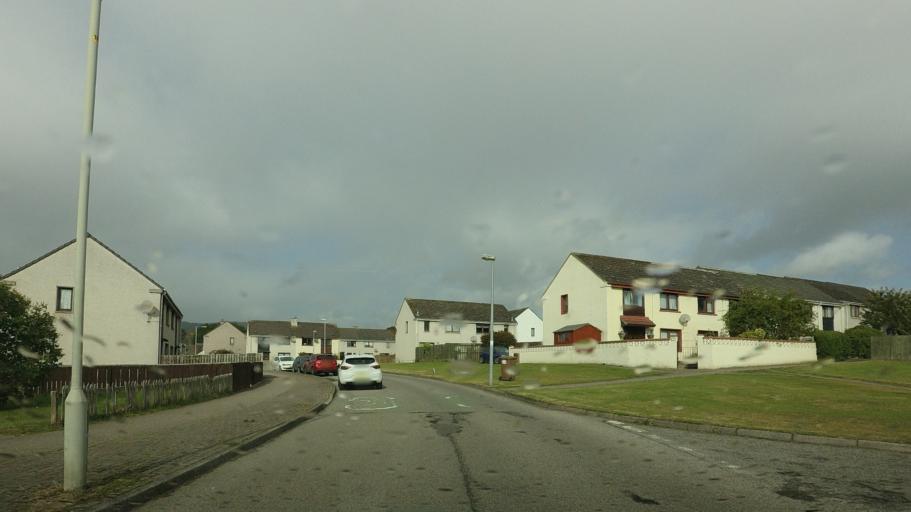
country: GB
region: Scotland
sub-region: Highland
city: Alness
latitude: 57.6944
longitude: -4.2683
